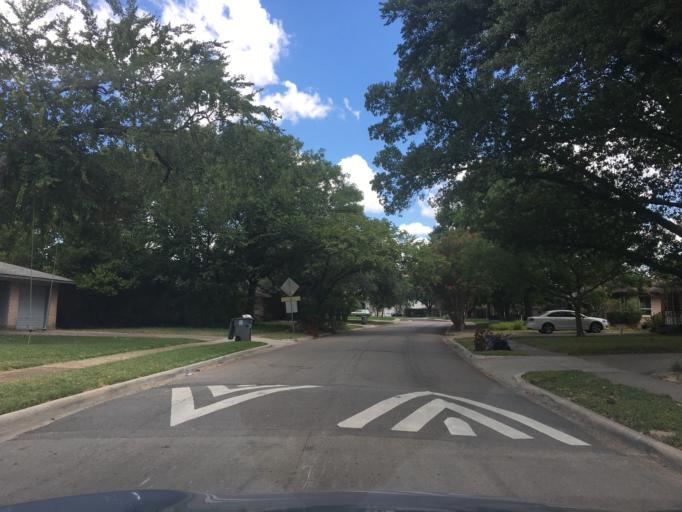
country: US
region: Texas
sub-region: Dallas County
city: Garland
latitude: 32.8707
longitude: -96.7062
